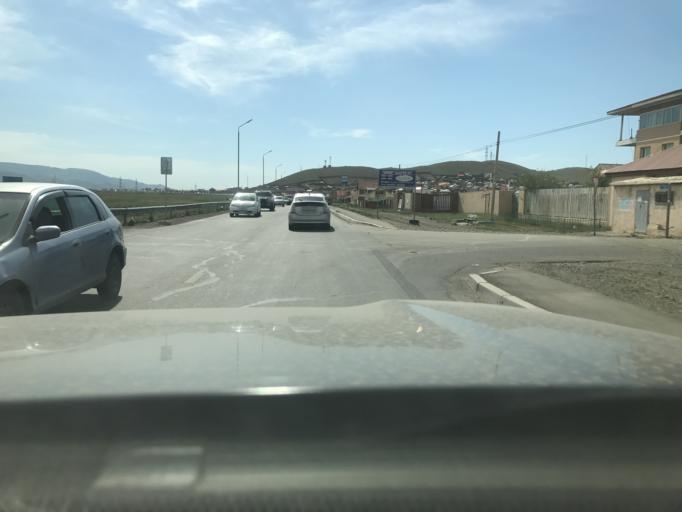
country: MN
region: Ulaanbaatar
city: Ulaanbaatar
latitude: 47.9155
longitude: 107.0633
